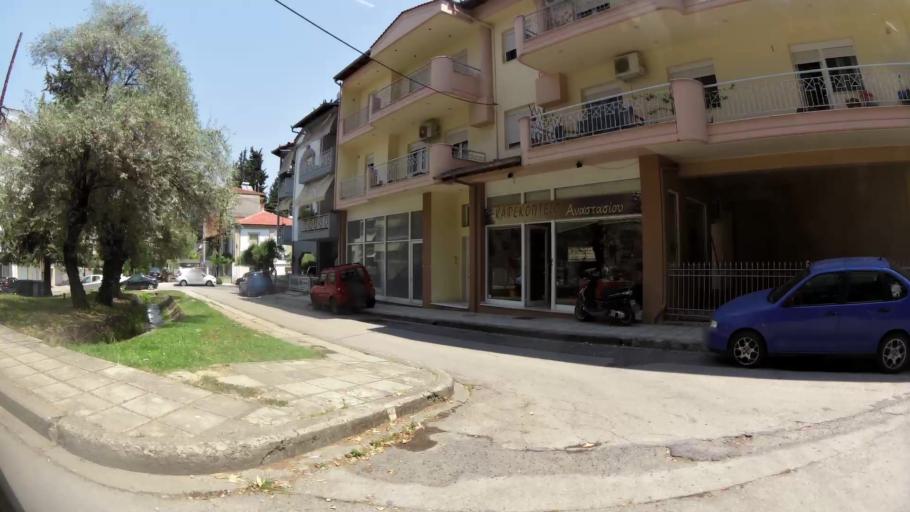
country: GR
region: Central Macedonia
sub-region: Nomos Imathias
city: Veroia
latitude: 40.5176
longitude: 22.1996
